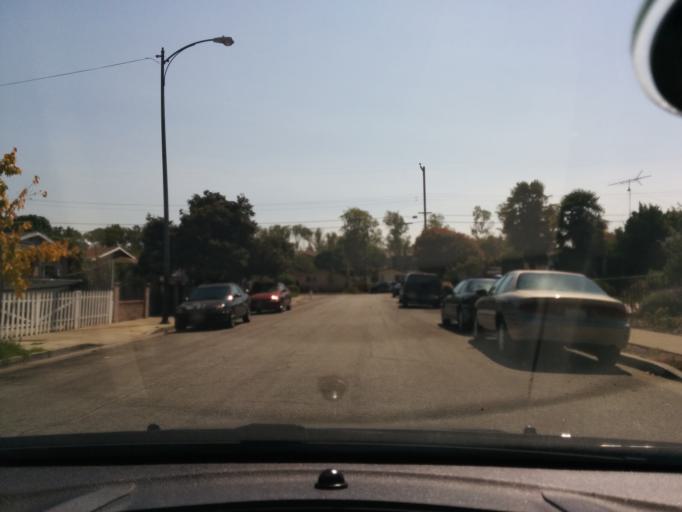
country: US
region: California
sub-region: Santa Clara County
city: Sunnyvale
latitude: 37.3900
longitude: -122.0013
